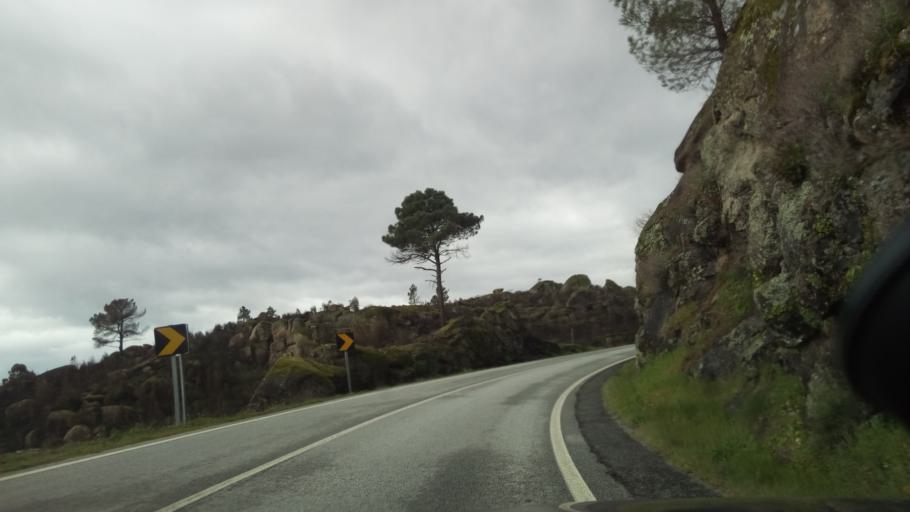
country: PT
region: Guarda
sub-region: Fornos de Algodres
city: Fornos de Algodres
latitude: 40.5576
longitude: -7.5632
